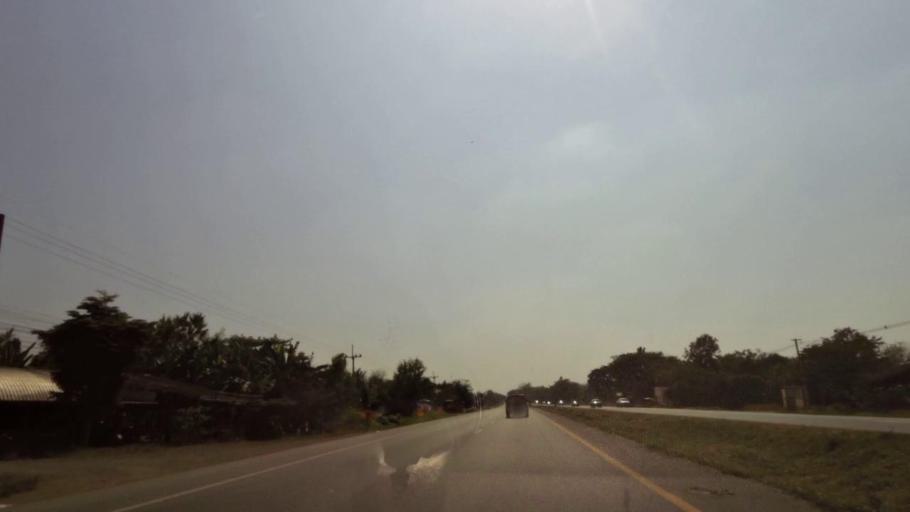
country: TH
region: Phichit
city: Bueng Na Rang
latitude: 16.3444
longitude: 100.1283
